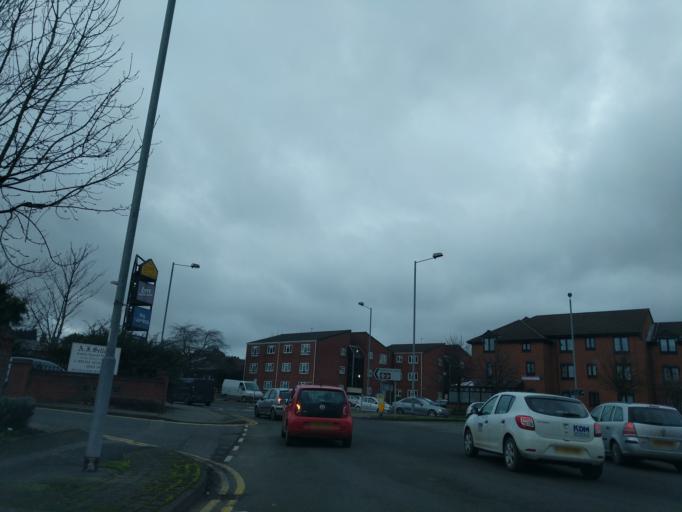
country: GB
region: England
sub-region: Staffordshire
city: Cannock
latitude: 52.6895
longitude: -2.0246
